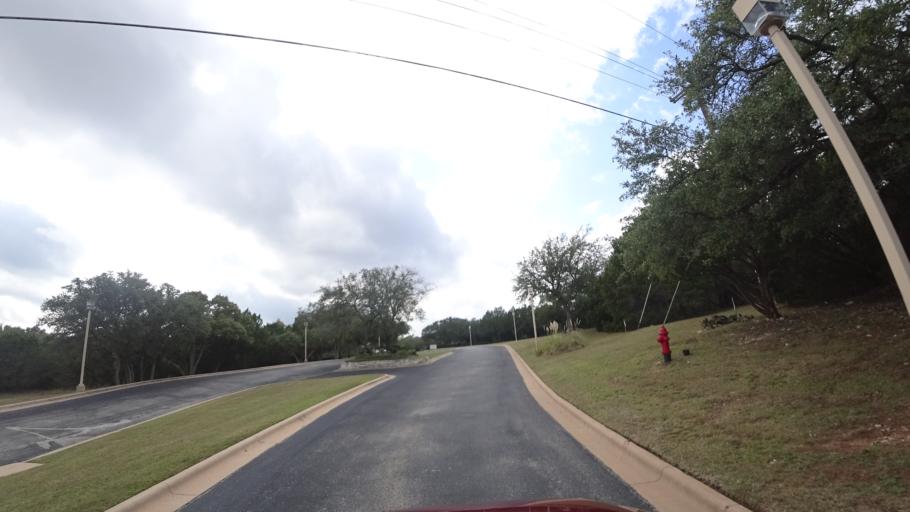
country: US
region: Texas
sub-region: Williamson County
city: Anderson Mill
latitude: 30.4191
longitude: -97.8529
